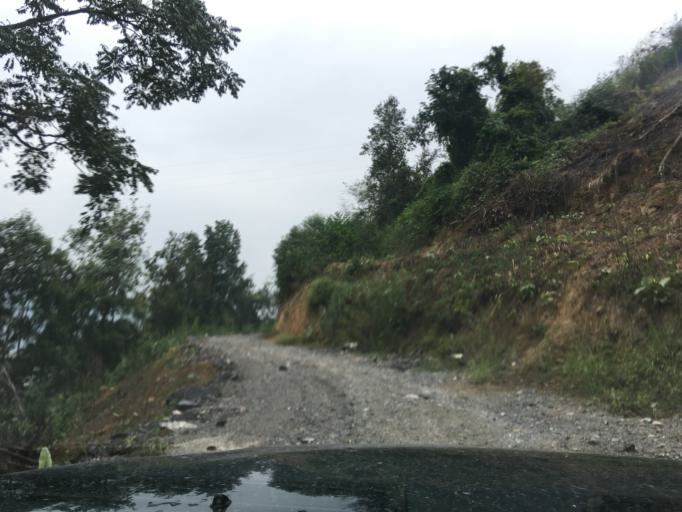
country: CN
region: Guangxi Zhuangzu Zizhiqu
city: Xinzhou
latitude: 25.0508
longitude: 105.9183
